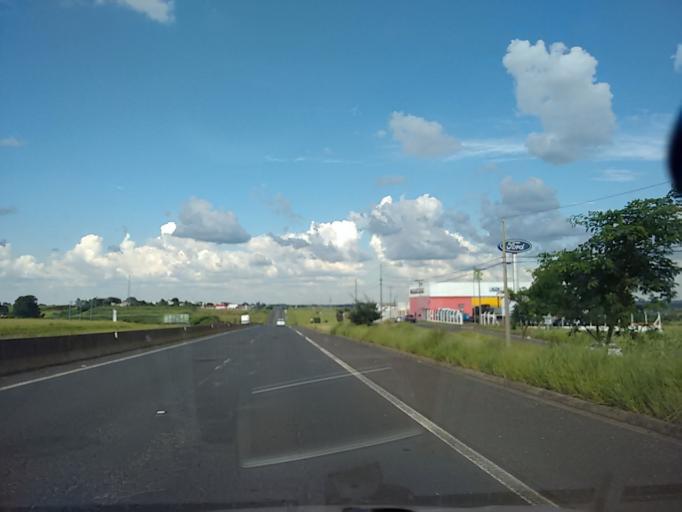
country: BR
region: Sao Paulo
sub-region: Marilia
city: Marilia
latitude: -22.2269
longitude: -49.8996
